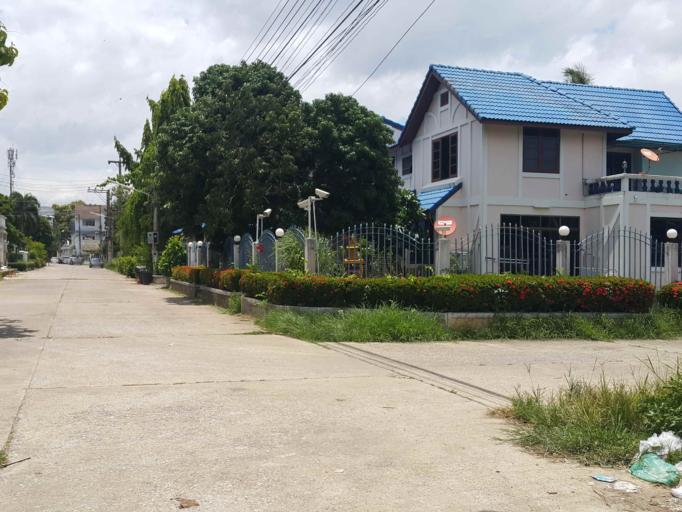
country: TH
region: Chiang Mai
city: Chiang Mai
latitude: 18.7615
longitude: 98.9923
